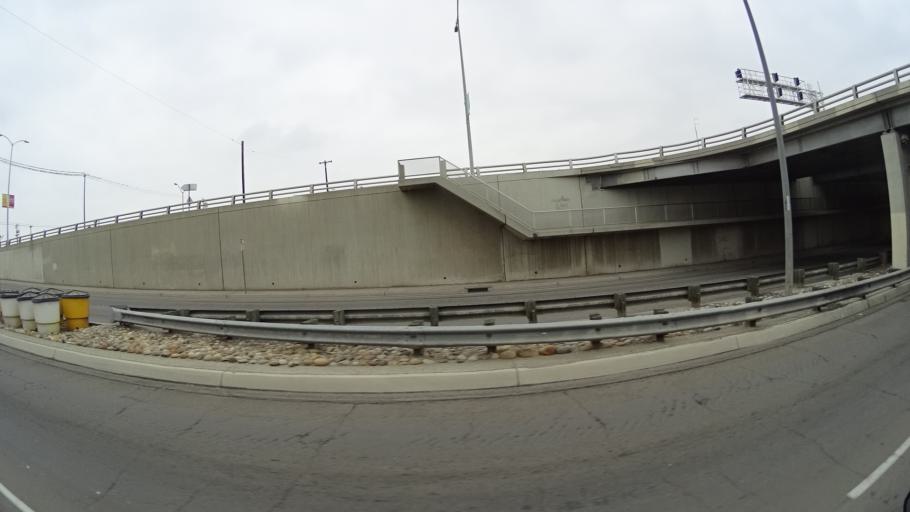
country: US
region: California
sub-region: Kern County
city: Bakersfield
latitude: 35.3711
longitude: -119.0188
